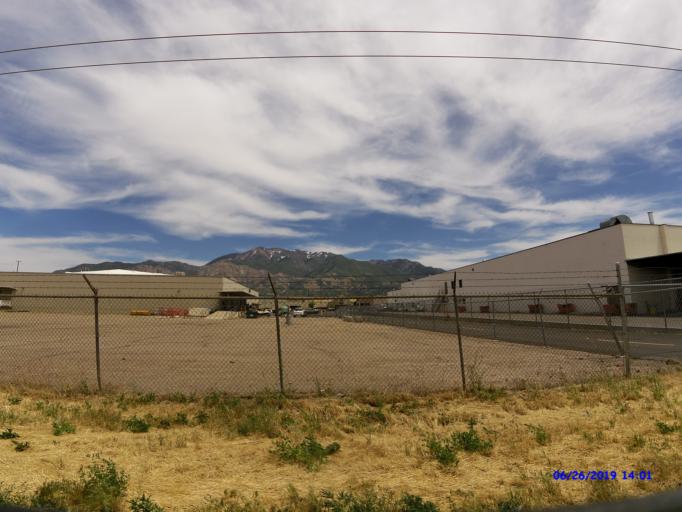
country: US
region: Utah
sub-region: Weber County
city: South Ogden
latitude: 41.1970
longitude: -111.9855
